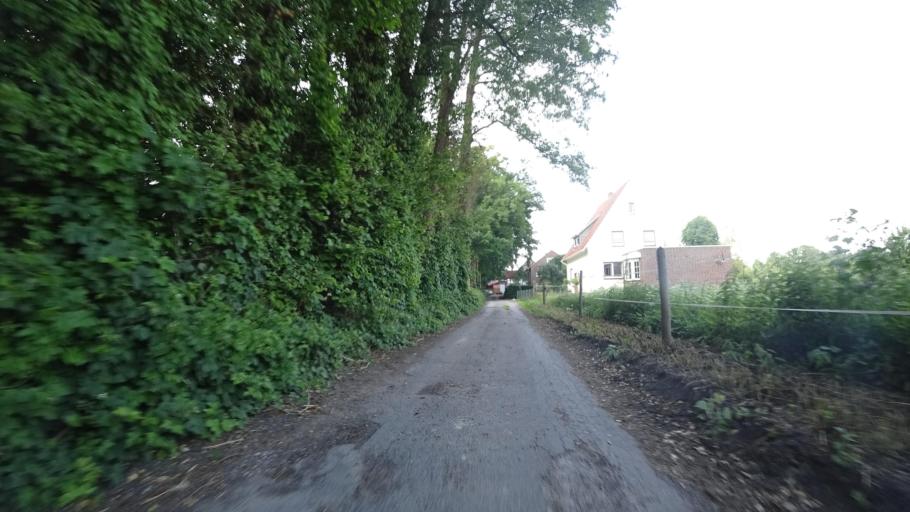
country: DE
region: North Rhine-Westphalia
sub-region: Regierungsbezirk Detmold
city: Guetersloh
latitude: 51.9154
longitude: 8.4479
